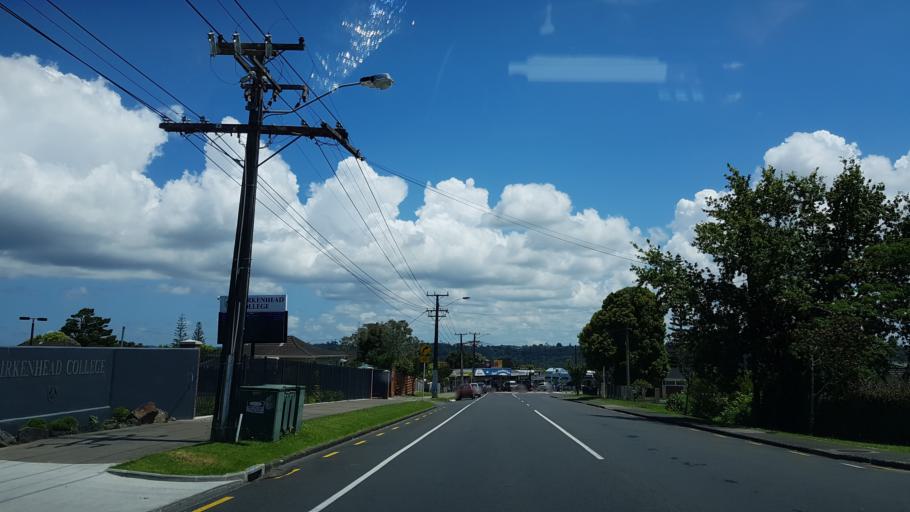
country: NZ
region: Auckland
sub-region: Auckland
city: North Shore
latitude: -36.7995
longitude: 174.7018
